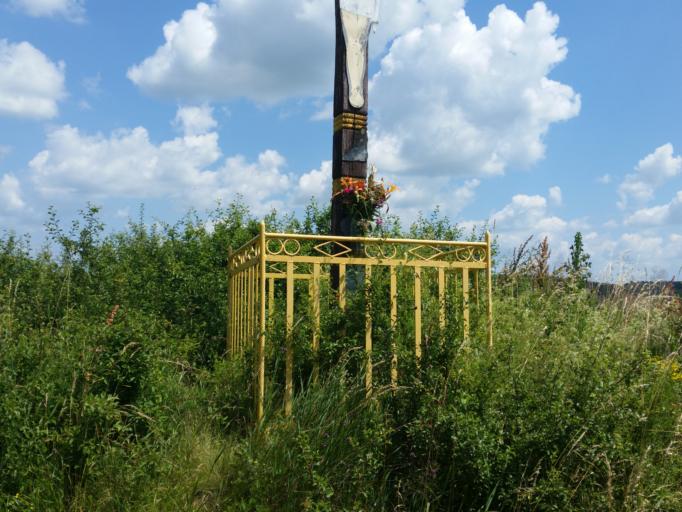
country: RO
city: Sanmartin
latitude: 46.9219
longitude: 23.5222
